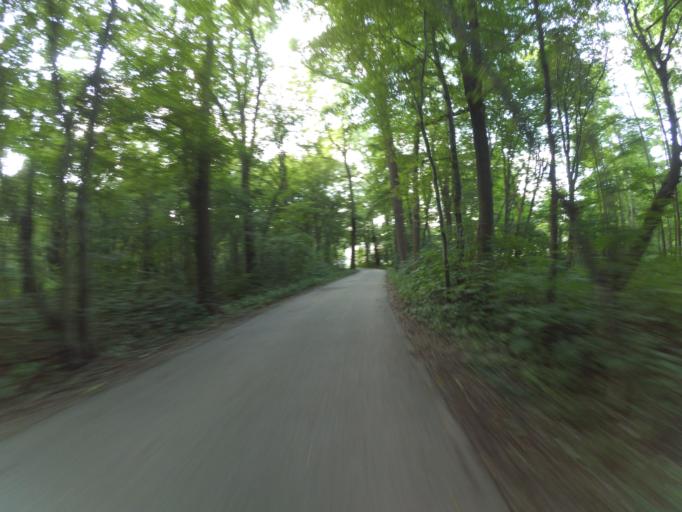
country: DE
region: Bavaria
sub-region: Upper Bavaria
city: Karlsfeld
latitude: 48.1898
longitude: 11.4827
